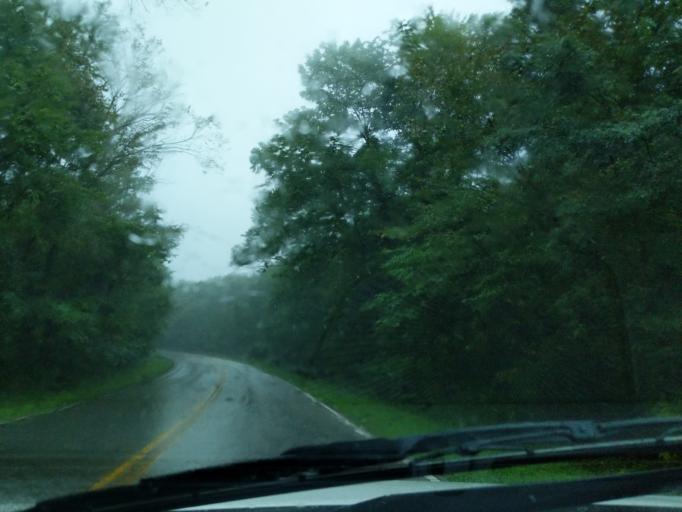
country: US
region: Kentucky
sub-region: Barren County
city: Cave City
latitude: 37.1377
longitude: -86.0726
